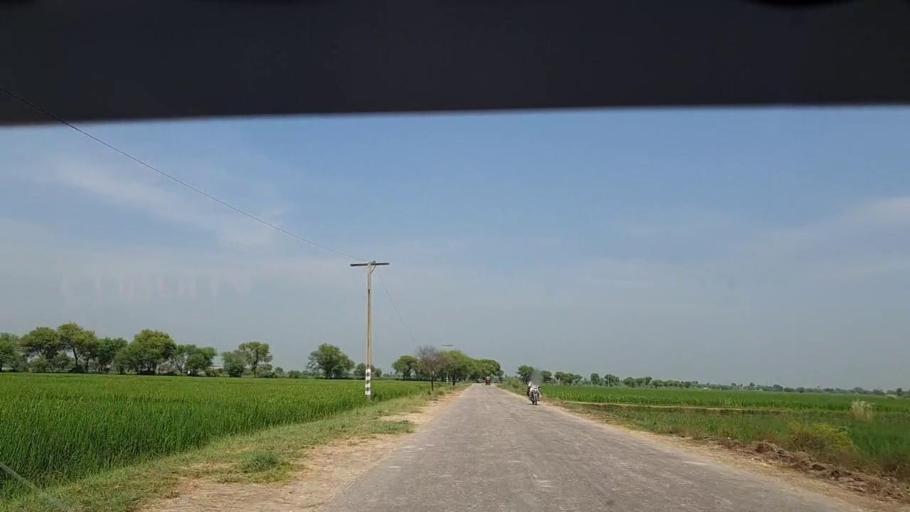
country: PK
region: Sindh
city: Thul
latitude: 28.1383
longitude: 68.7162
